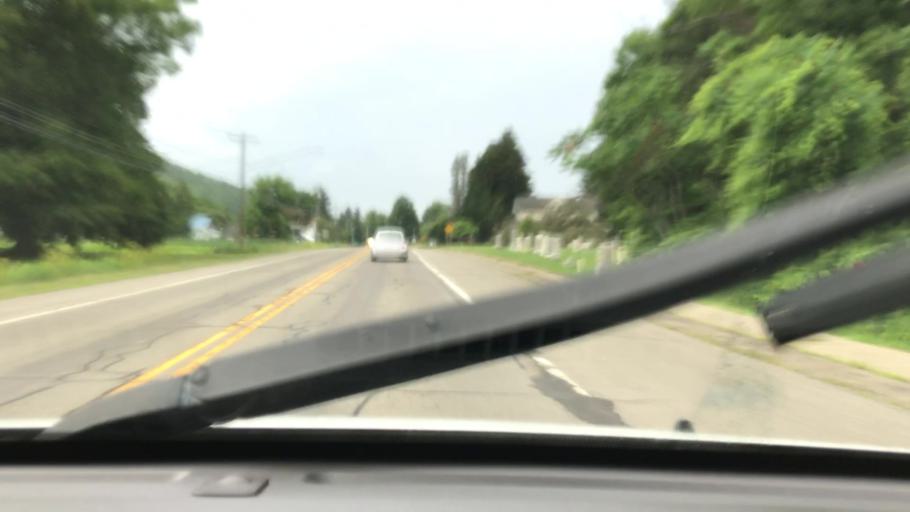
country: US
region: New York
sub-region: Cattaraugus County
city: Salamanca
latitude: 42.2188
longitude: -78.6370
